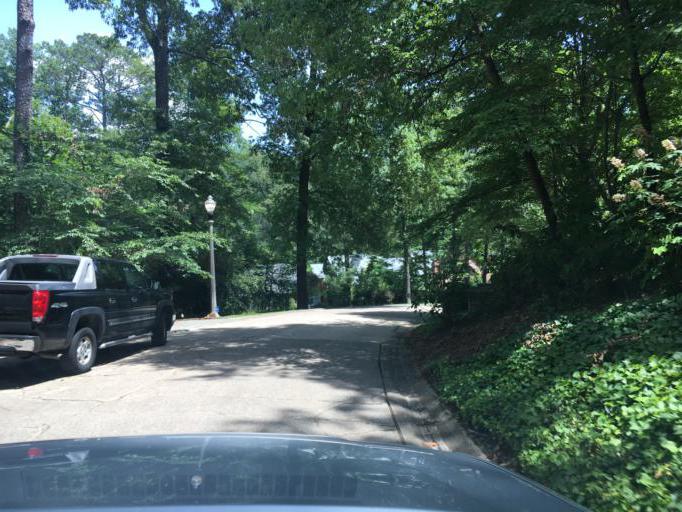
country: US
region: Alabama
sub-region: Jefferson County
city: Mountain Brook
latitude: 33.4805
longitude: -86.7623
